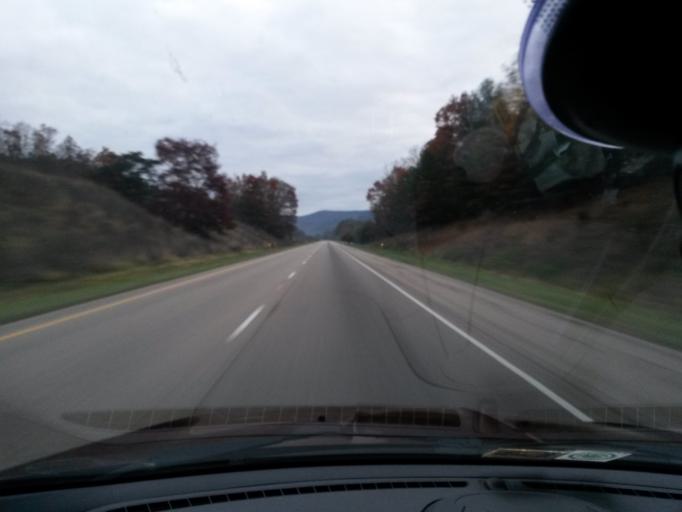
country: US
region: Virginia
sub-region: Alleghany County
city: Clifton Forge
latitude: 37.8024
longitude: -79.7017
